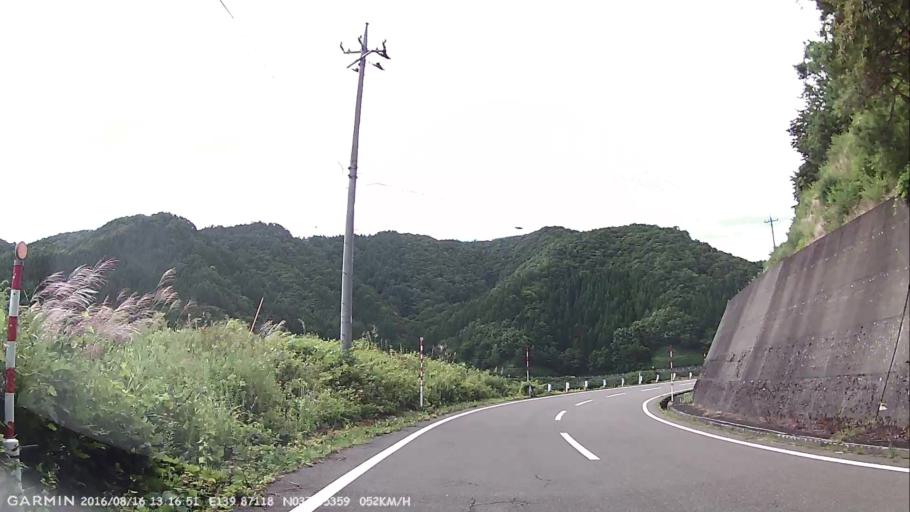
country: JP
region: Fukushima
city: Kitakata
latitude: 37.3536
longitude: 139.8712
